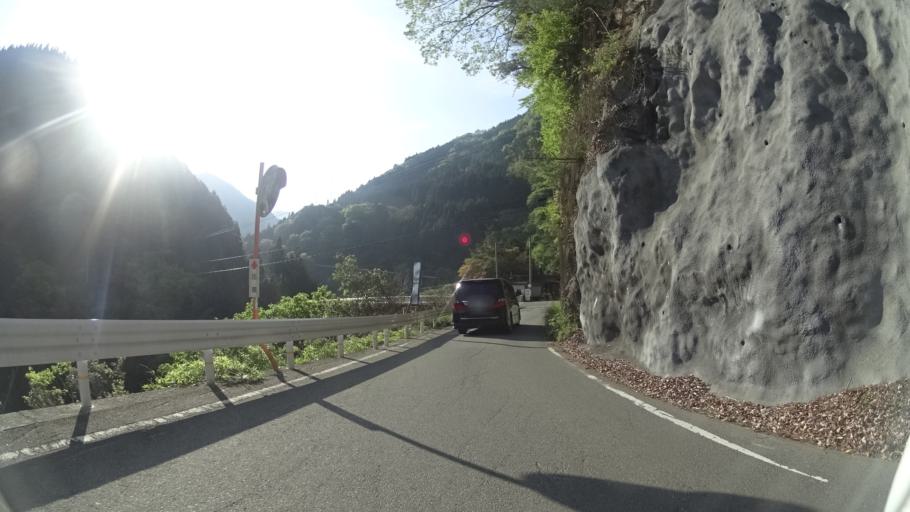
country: JP
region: Tokushima
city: Ikedacho
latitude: 33.8797
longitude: 133.8687
